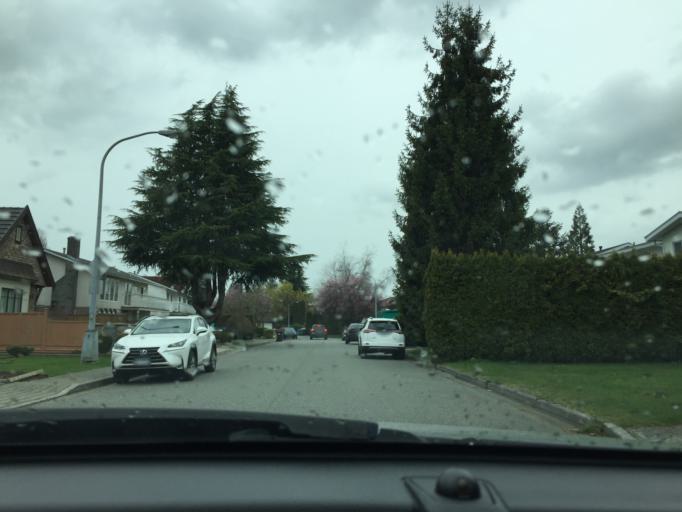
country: CA
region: British Columbia
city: Richmond
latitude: 49.1467
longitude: -123.1266
